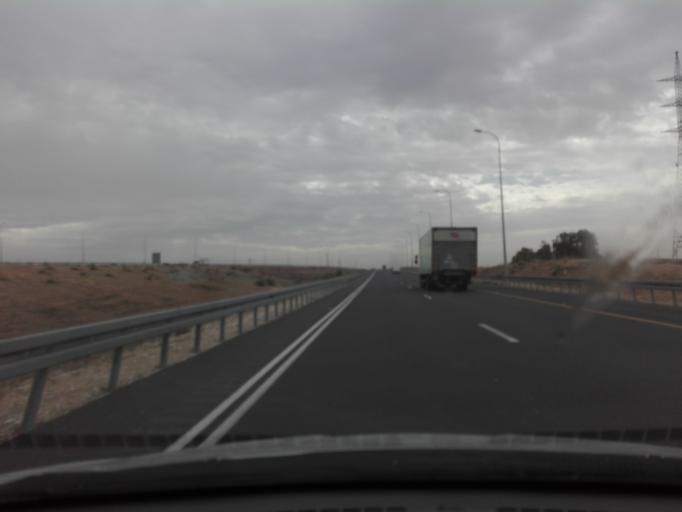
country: IL
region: Southern District
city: Lehavim
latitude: 31.3950
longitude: 34.7890
